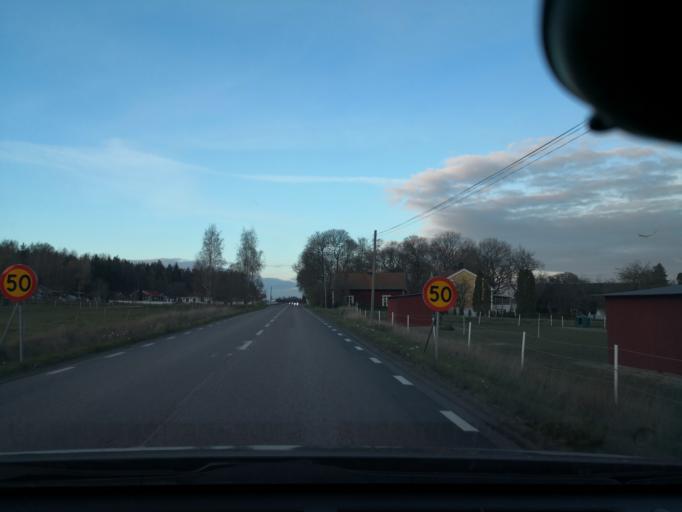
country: SE
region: Vaestmanland
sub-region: Vasteras
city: Tillberga
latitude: 59.6442
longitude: 16.6808
